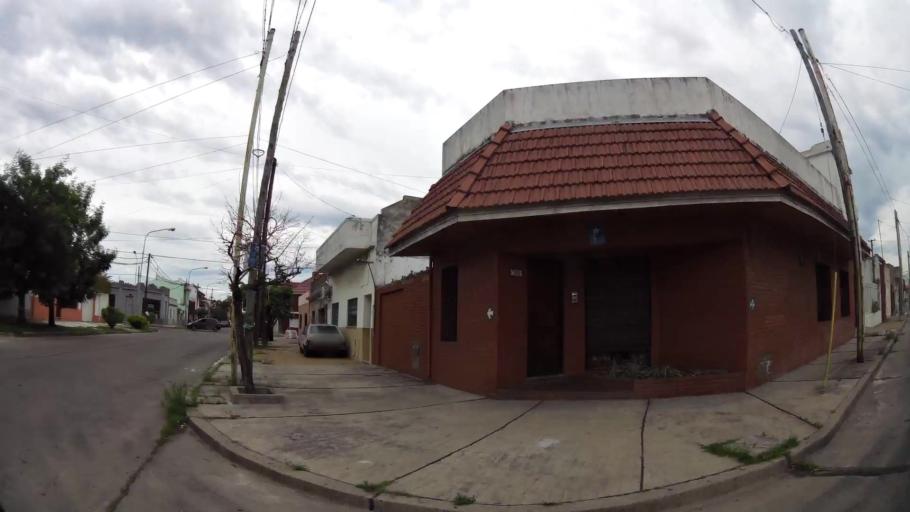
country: AR
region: Buenos Aires
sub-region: Partido de Lanus
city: Lanus
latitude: -34.6793
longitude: -58.4007
